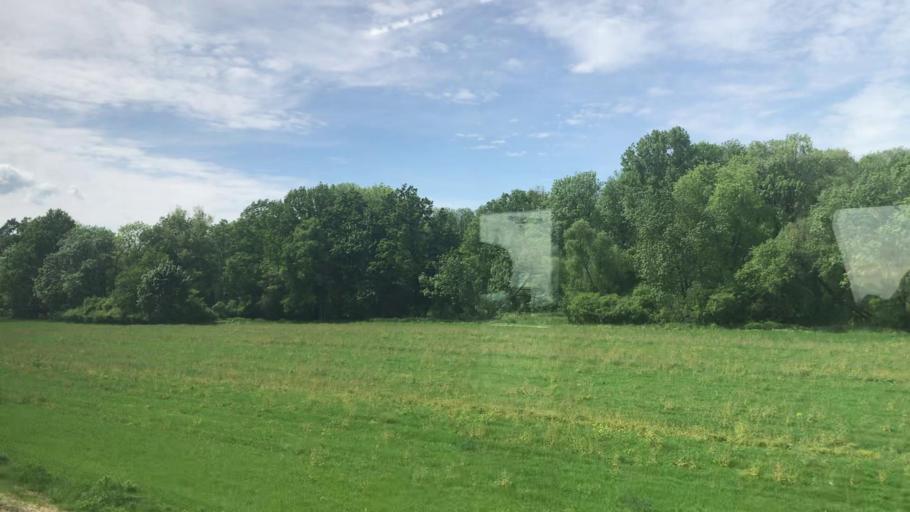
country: PL
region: Lower Silesian Voivodeship
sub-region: Powiat wroclawski
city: Sobotka
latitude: 50.9831
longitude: 16.6507
